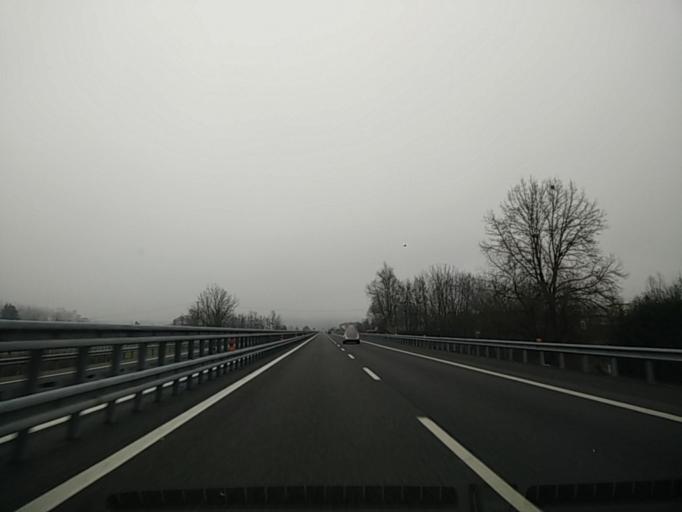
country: IT
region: Piedmont
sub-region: Provincia di Asti
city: Baldichieri d'Asti
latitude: 44.9033
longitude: 8.0820
